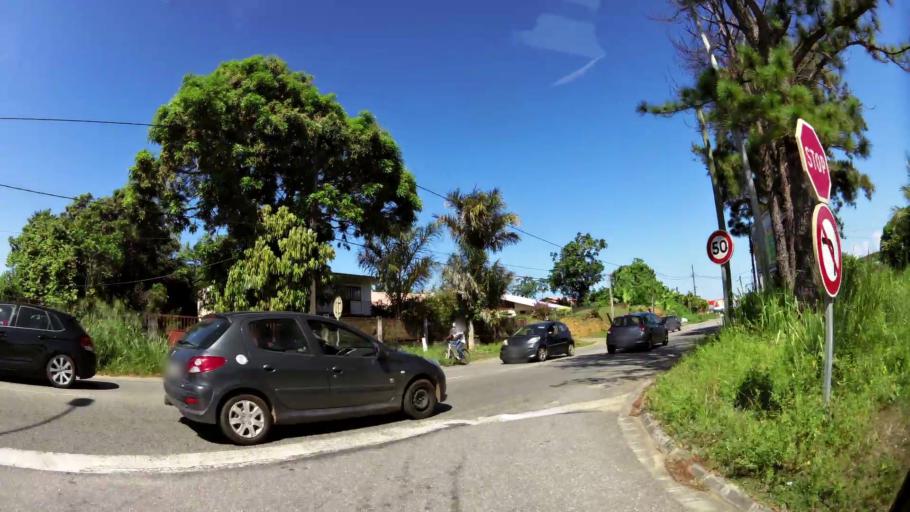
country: GF
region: Guyane
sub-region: Guyane
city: Remire-Montjoly
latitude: 4.9160
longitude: -52.2757
